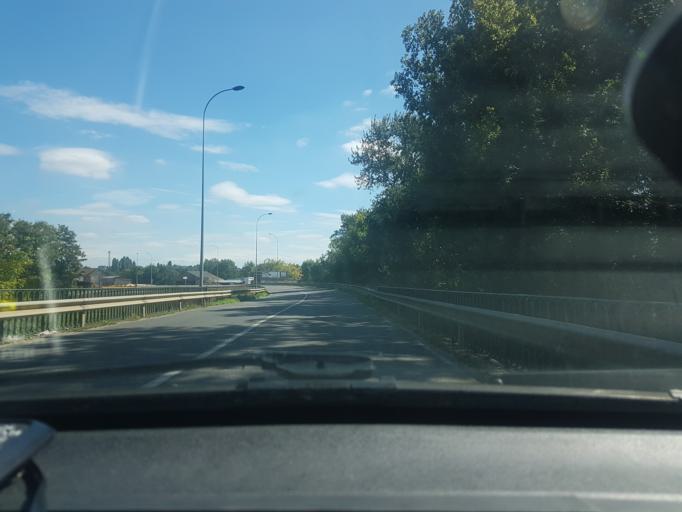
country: FR
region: Franche-Comte
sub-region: Departement de la Haute-Saone
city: Gray-la-Ville
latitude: 47.4489
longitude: 5.5642
